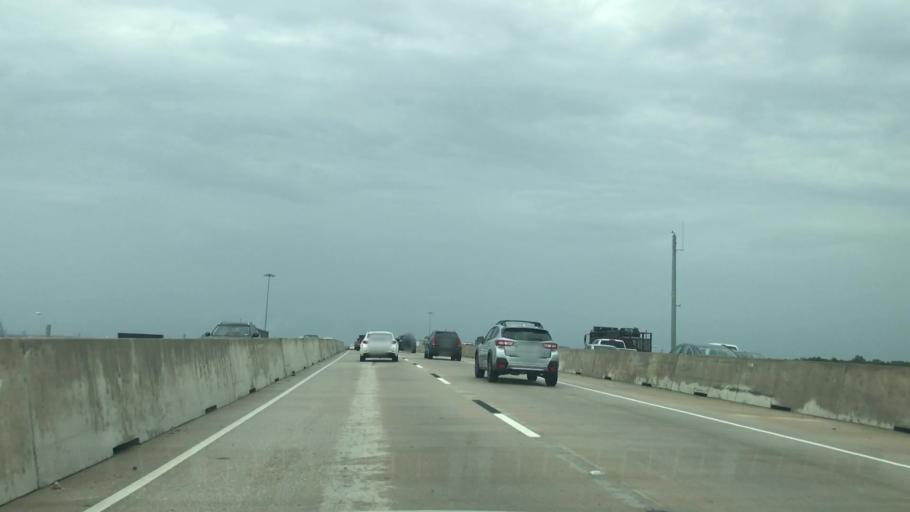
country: US
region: Texas
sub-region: Dallas County
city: Carrollton
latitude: 32.9525
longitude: -96.9101
